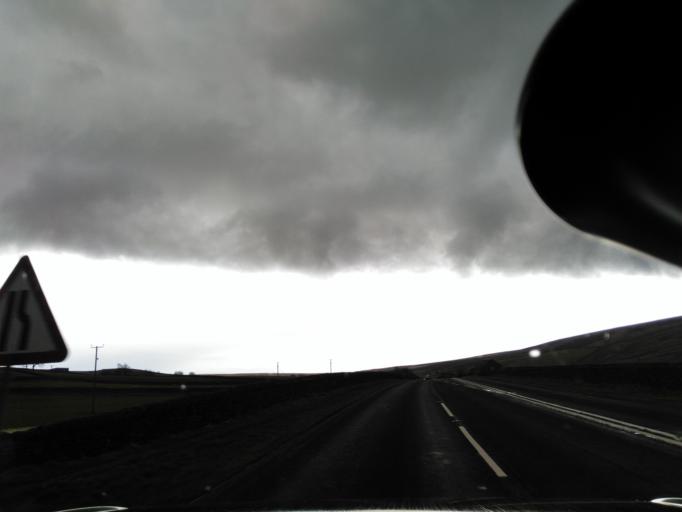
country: GB
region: England
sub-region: Bradford
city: Addingham
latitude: 53.9862
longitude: -1.8415
